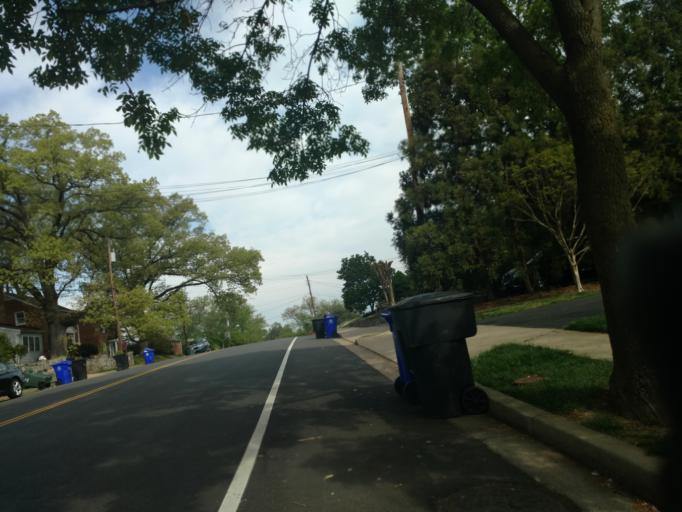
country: US
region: Virginia
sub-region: Fairfax County
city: Seven Corners
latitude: 38.8948
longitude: -77.1352
